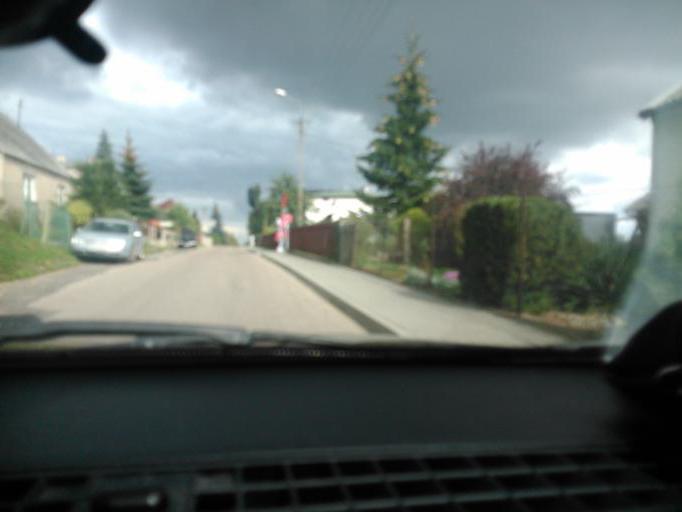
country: PL
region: Kujawsko-Pomorskie
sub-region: Powiat brodnicki
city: Swiedziebnia
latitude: 53.2165
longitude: 19.5219
